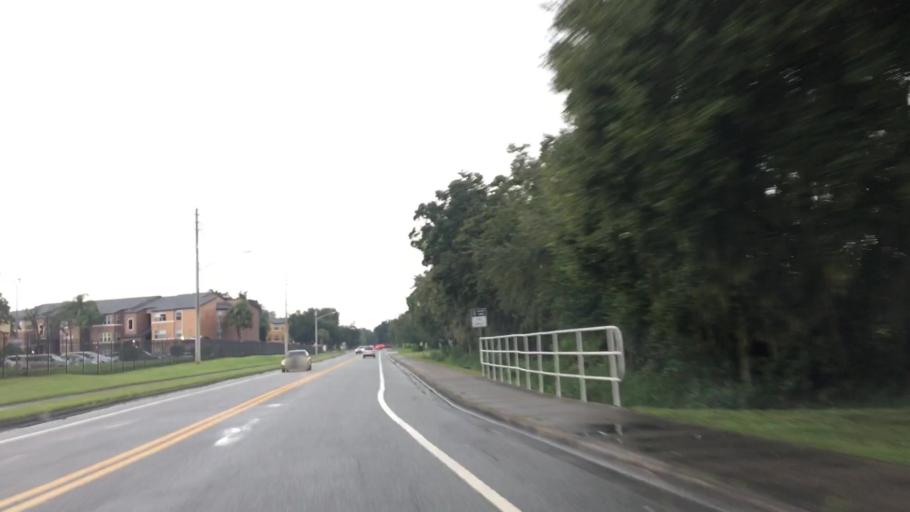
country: US
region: Florida
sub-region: Orange County
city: Conway
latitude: 28.4954
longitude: -81.3062
